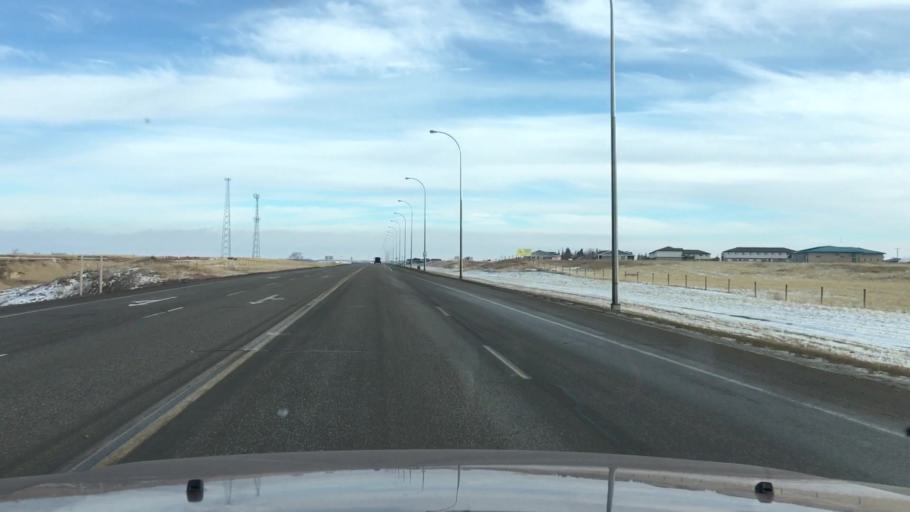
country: CA
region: Saskatchewan
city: Pilot Butte
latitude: 50.4855
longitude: -104.4339
